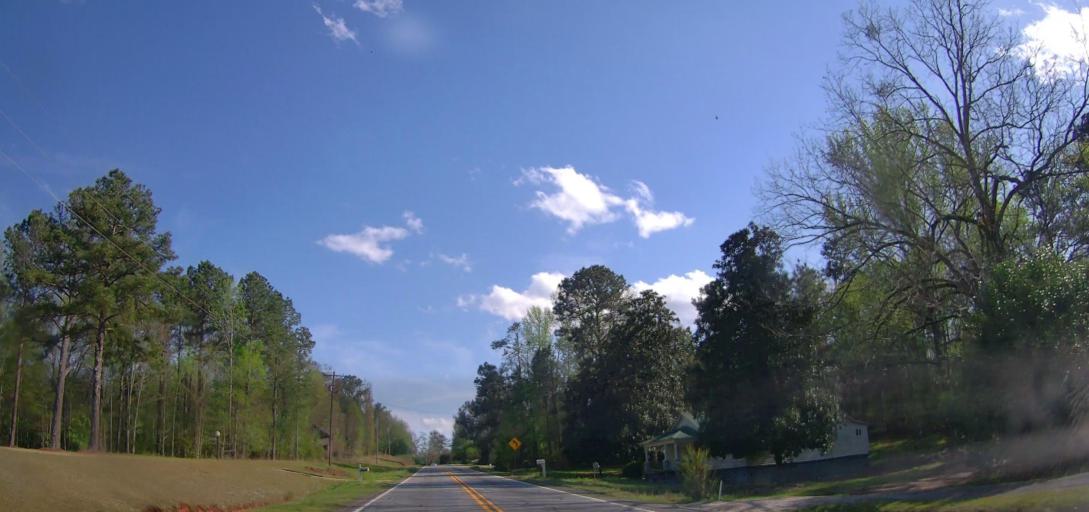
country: US
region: Georgia
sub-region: Baldwin County
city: Hardwick
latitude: 33.0860
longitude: -83.1715
